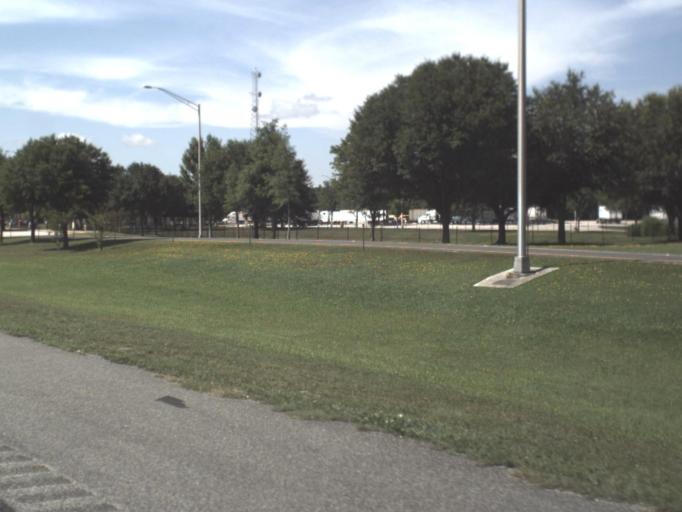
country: US
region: Florida
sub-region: Saint Johns County
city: Palm Valley
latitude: 30.0966
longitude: -81.4990
